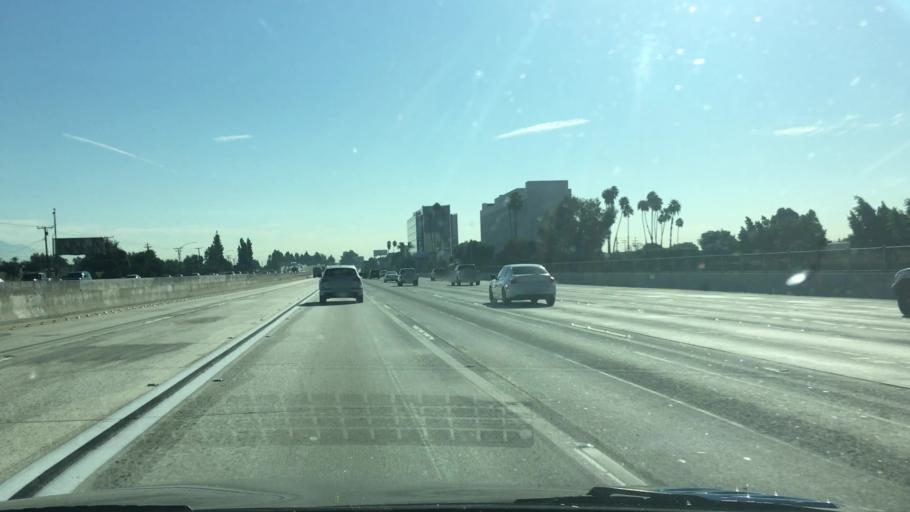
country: US
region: California
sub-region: Los Angeles County
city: Rosemead
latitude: 34.0723
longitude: -118.0642
